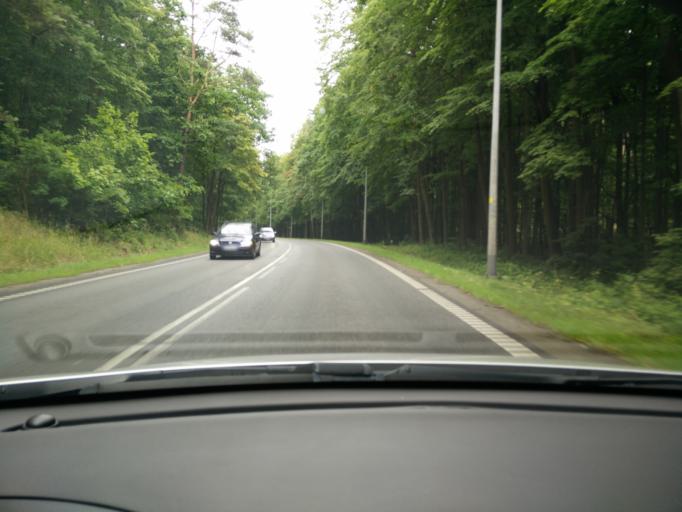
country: PL
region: Pomeranian Voivodeship
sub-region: Sopot
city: Sopot
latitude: 54.4211
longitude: 18.5182
